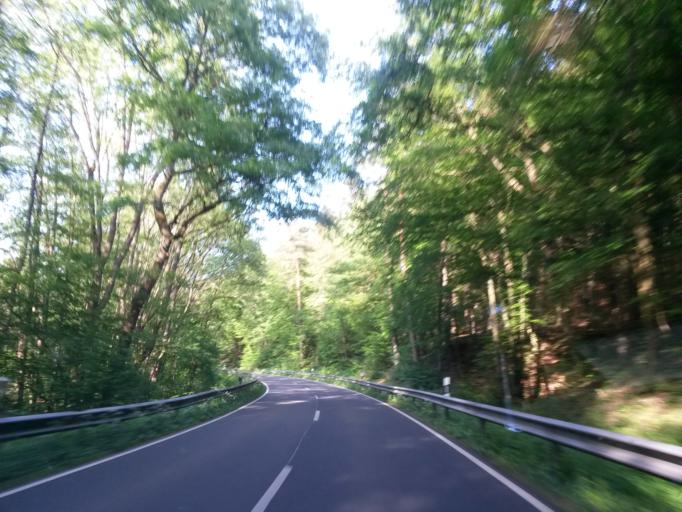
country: DE
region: North Rhine-Westphalia
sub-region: Regierungsbezirk Koln
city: Much
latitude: 50.8703
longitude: 7.3482
